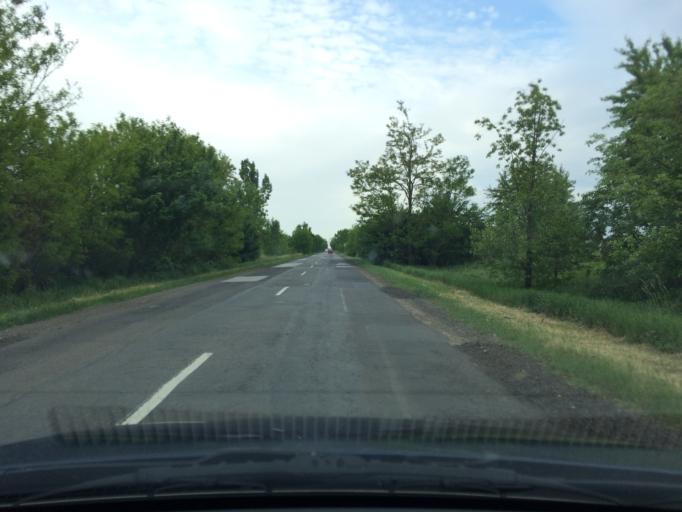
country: HU
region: Szabolcs-Szatmar-Bereg
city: Tiszavasvari
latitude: 47.9158
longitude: 21.3971
